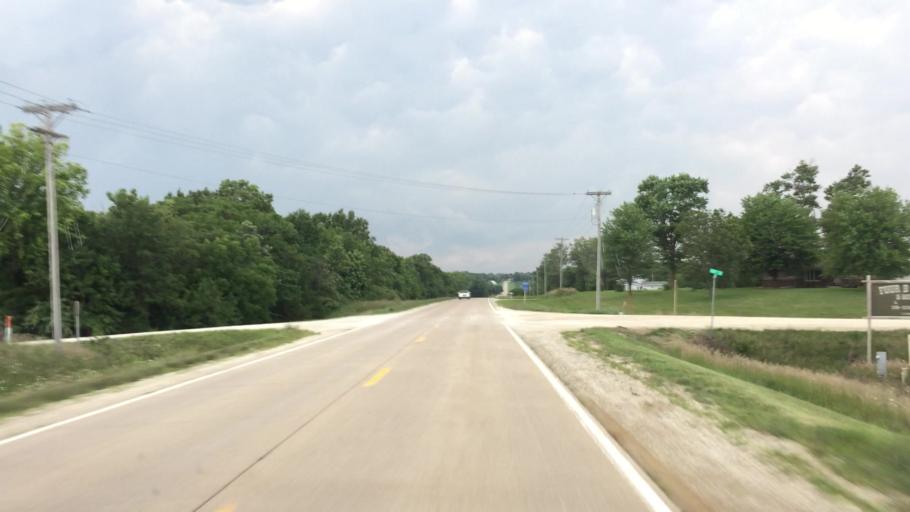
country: US
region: Iowa
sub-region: Lee County
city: Fort Madison
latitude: 40.7104
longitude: -91.3300
